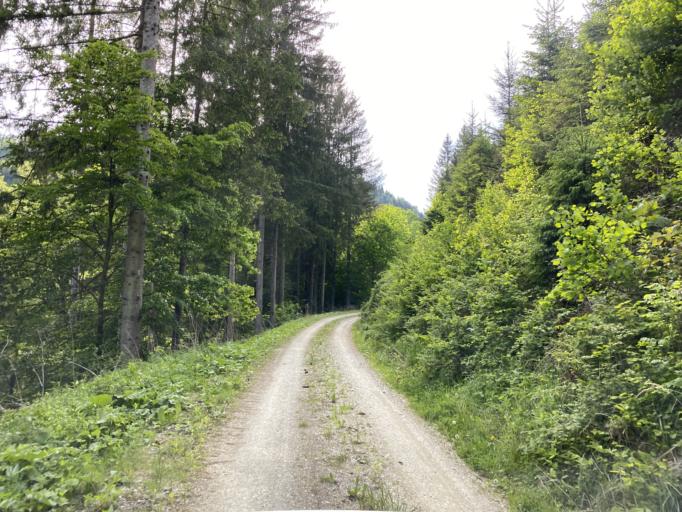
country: AT
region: Styria
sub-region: Politischer Bezirk Weiz
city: Koglhof
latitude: 47.3134
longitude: 15.6516
